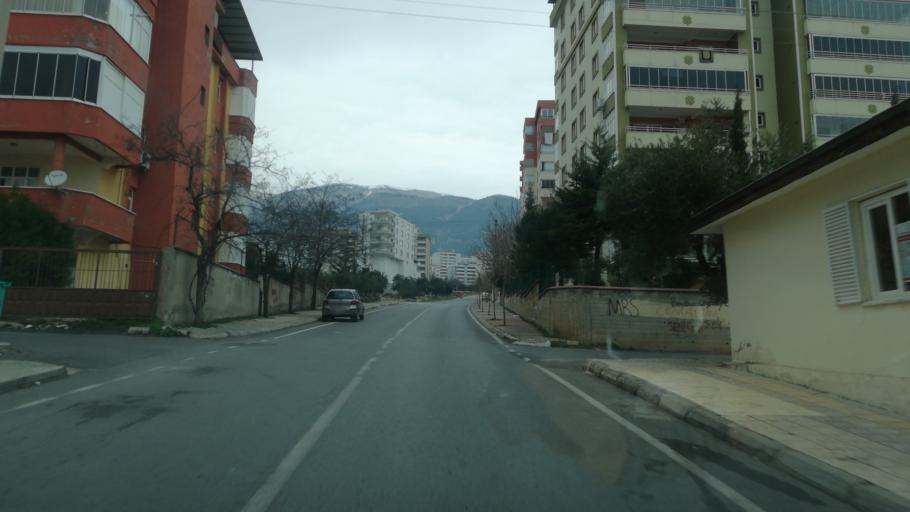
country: TR
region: Kahramanmaras
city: Kahramanmaras
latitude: 37.5923
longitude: 36.8934
